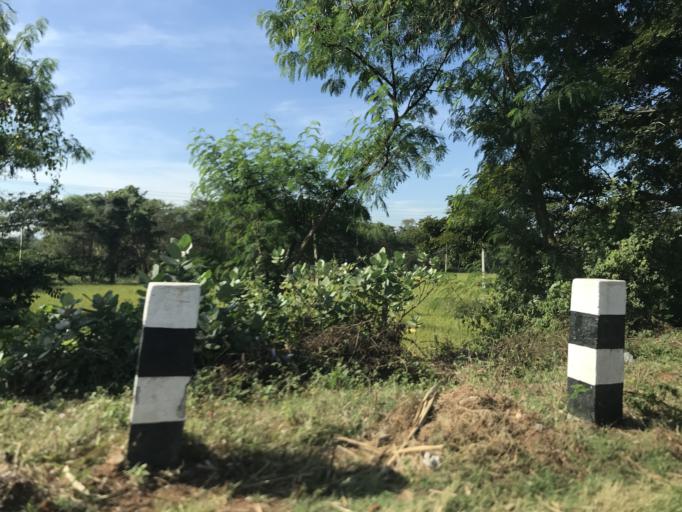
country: IN
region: Karnataka
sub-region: Mysore
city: Heggadadevankote
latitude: 12.1260
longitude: 76.4542
